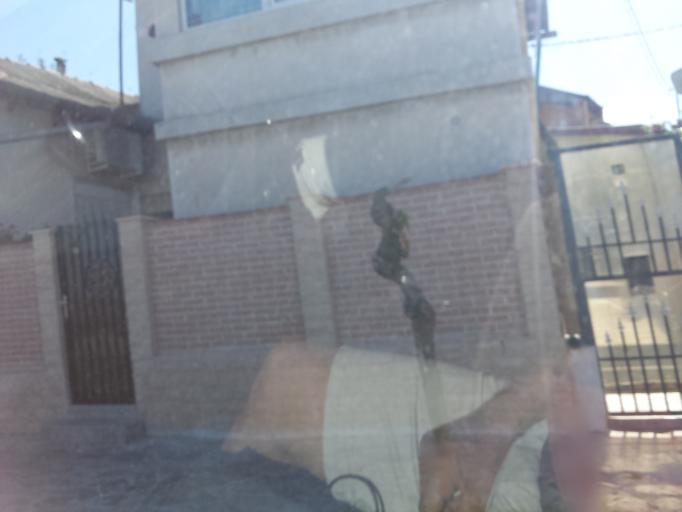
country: RO
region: Tulcea
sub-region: Municipiul Tulcea
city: Tulcea
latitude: 45.1826
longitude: 28.8098
